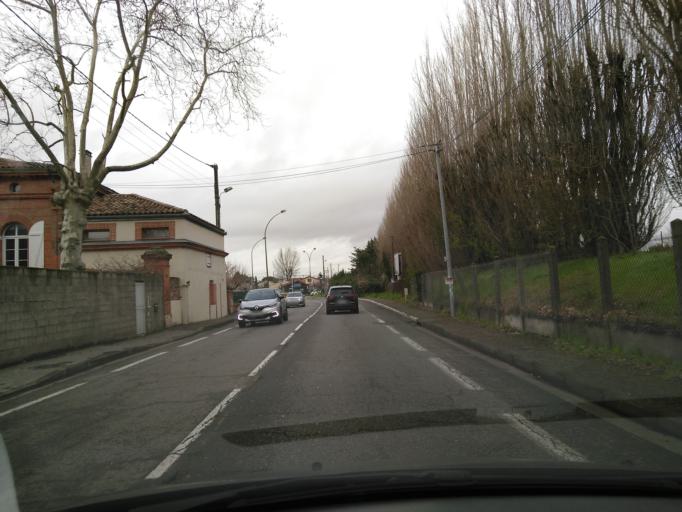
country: FR
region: Midi-Pyrenees
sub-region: Departement de la Haute-Garonne
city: Toulouse
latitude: 43.6328
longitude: 1.4386
